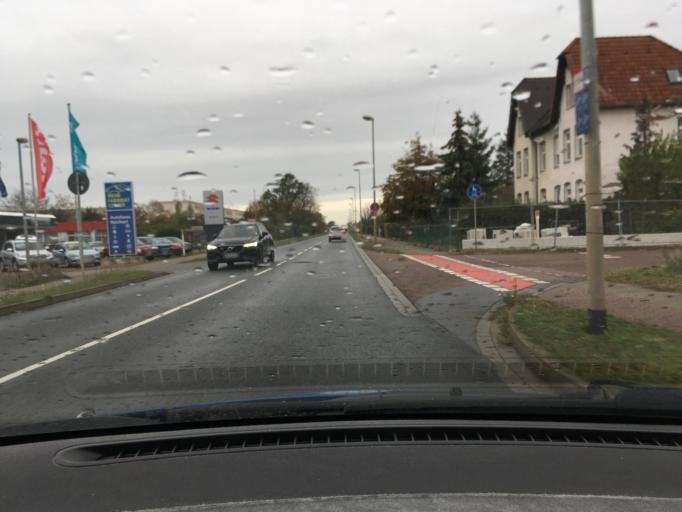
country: DE
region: Saxony-Anhalt
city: Rosslau
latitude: 51.8910
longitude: 12.2276
